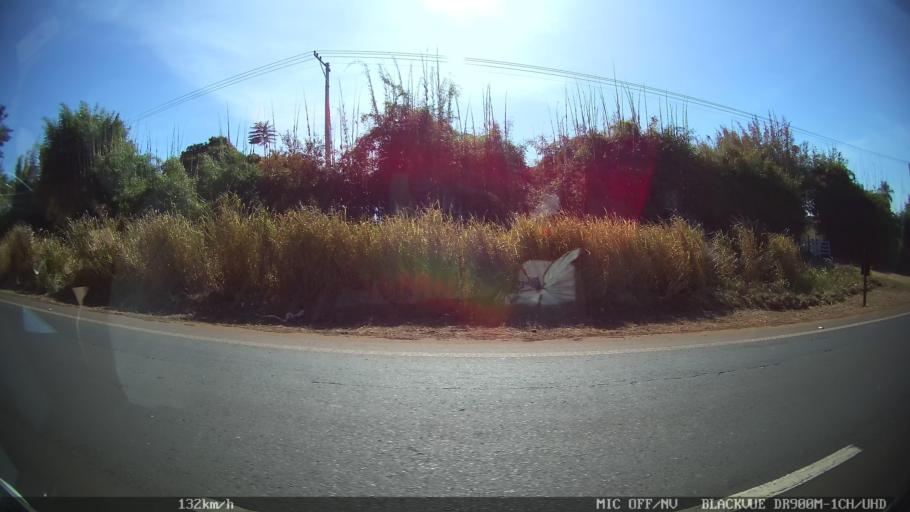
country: BR
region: Sao Paulo
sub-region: Barretos
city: Barretos
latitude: -20.5490
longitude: -48.6305
